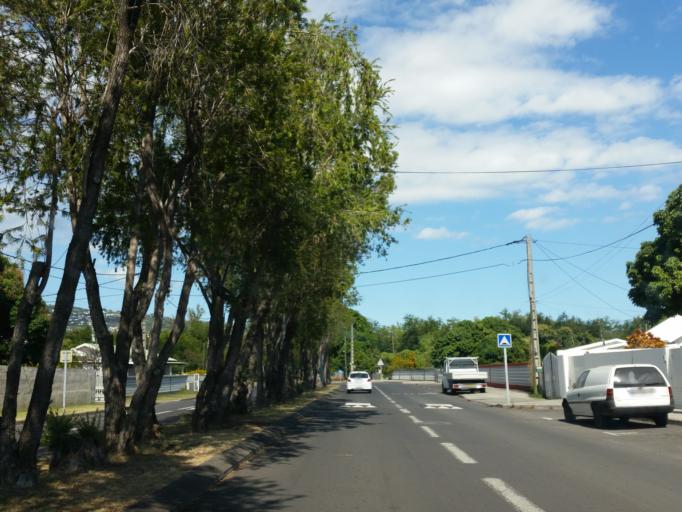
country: RE
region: Reunion
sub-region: Reunion
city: Saint-Paul
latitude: -20.9859
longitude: 55.2885
